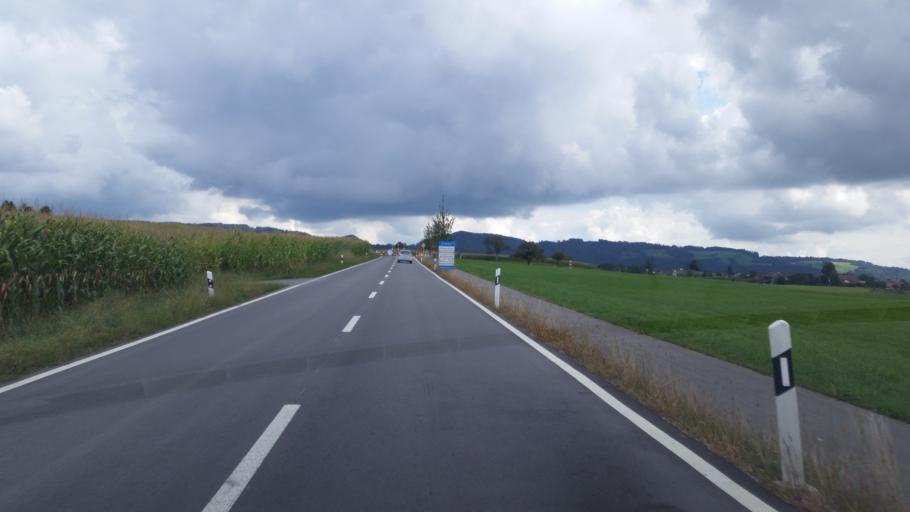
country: CH
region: Zurich
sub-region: Bezirk Affoltern
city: Mettmenstetten
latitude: 47.2427
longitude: 8.4796
